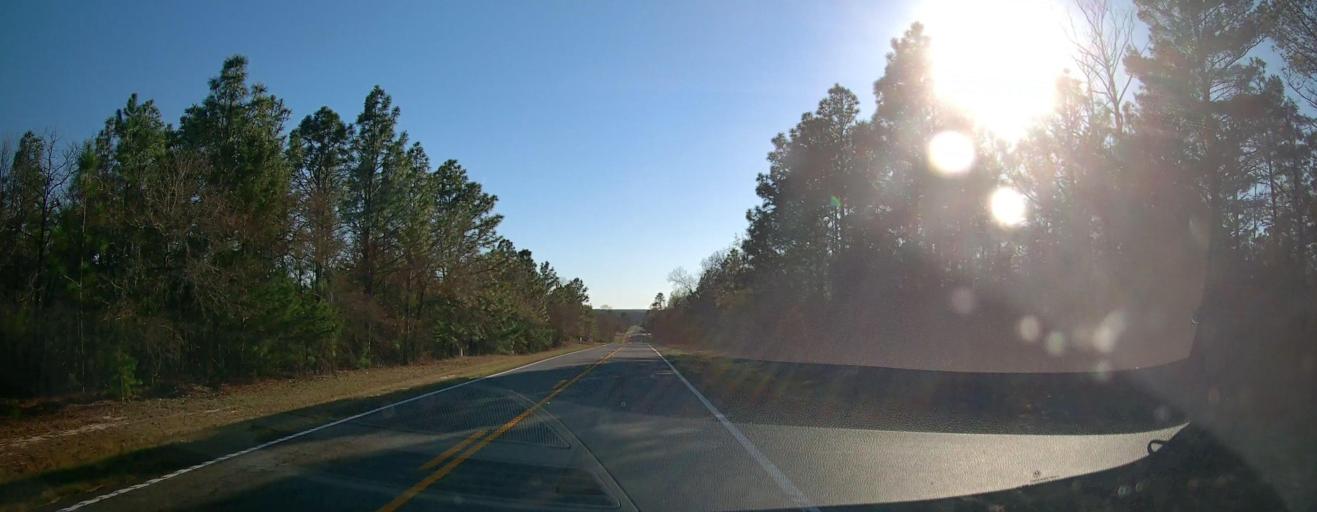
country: US
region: Georgia
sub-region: Taylor County
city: Butler
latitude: 32.5353
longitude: -84.2958
